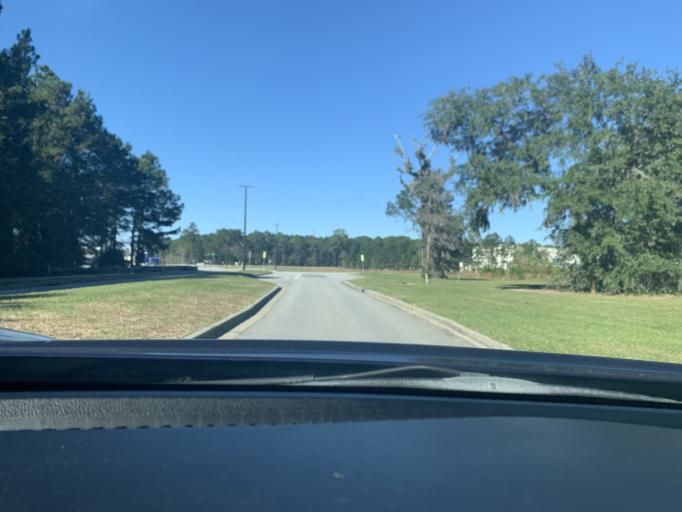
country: US
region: Georgia
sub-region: Chatham County
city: Pooler
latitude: 32.0866
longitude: -81.2745
